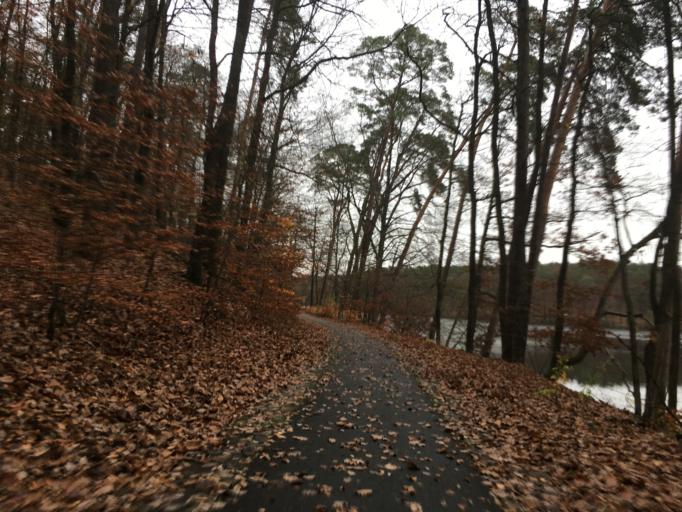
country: DE
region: Brandenburg
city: Mixdorf
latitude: 52.1583
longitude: 14.4432
